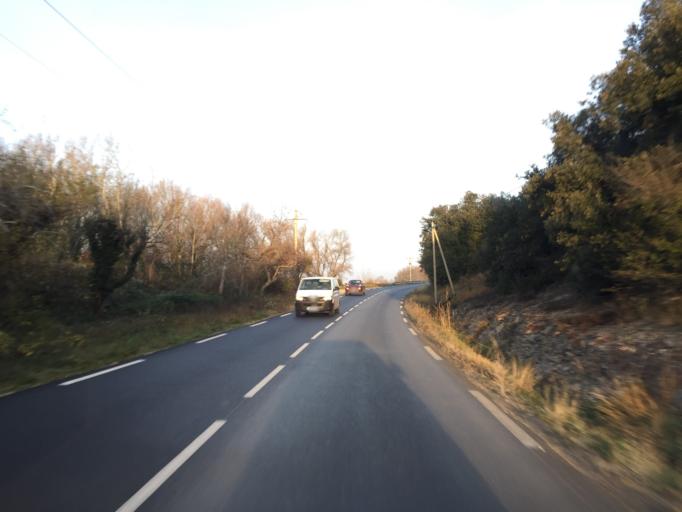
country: FR
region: Languedoc-Roussillon
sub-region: Departement du Gard
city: Roquemaure
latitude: 44.0660
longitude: 4.7915
